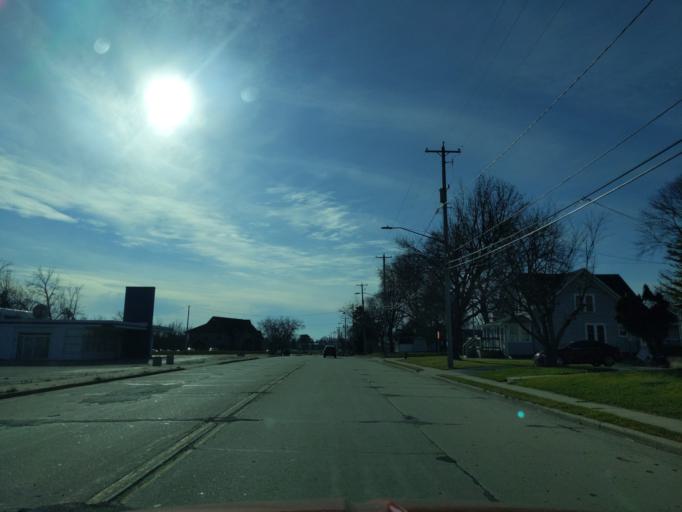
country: US
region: Wisconsin
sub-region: Walworth County
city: Whitewater
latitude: 42.8267
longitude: -88.7433
